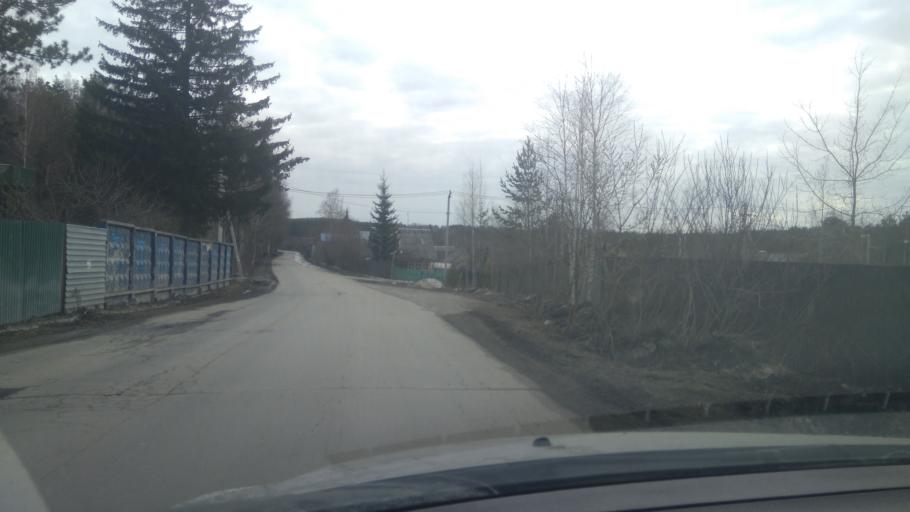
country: RU
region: Sverdlovsk
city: Severka
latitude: 56.8464
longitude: 60.3832
